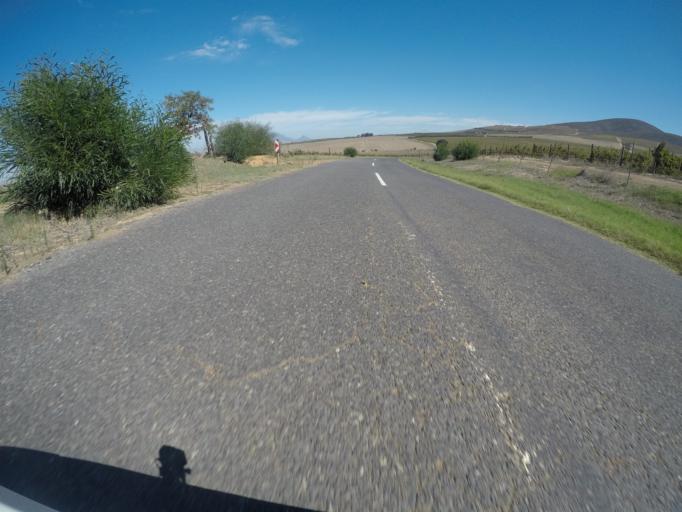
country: ZA
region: Western Cape
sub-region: City of Cape Town
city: Sunset Beach
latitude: -33.7171
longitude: 18.5816
